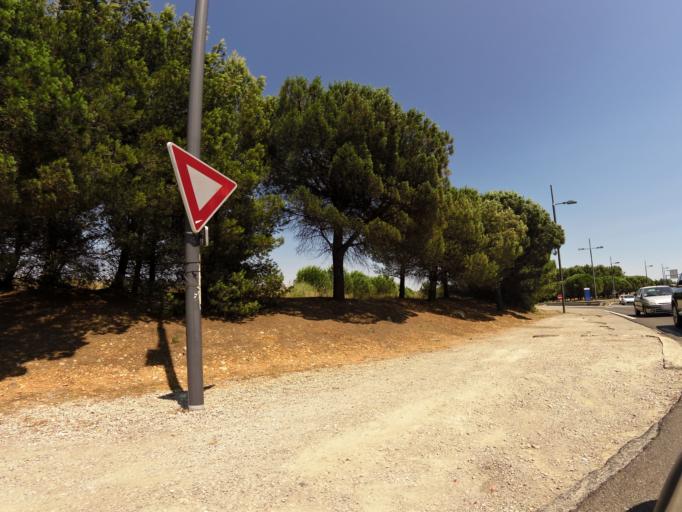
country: FR
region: Languedoc-Roussillon
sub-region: Departement de l'Herault
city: Castelnau-le-Lez
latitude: 43.6080
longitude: 3.9310
